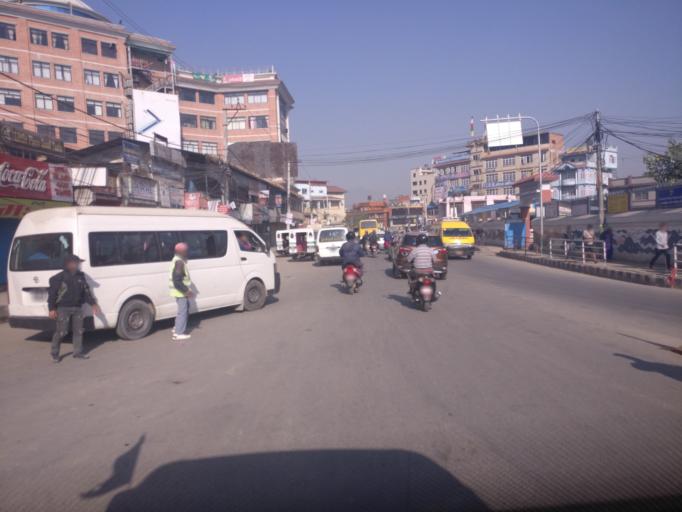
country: NP
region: Central Region
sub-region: Bagmati Zone
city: Patan
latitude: 27.6672
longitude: 85.3224
